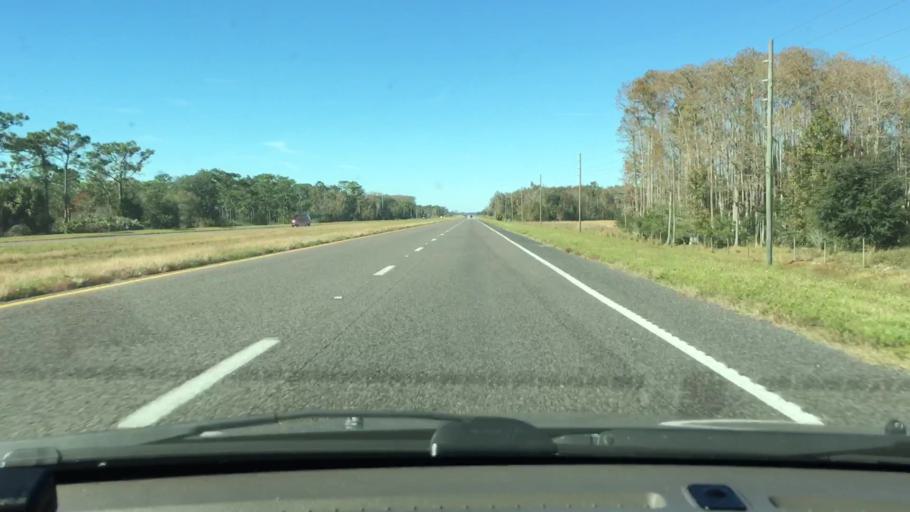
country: US
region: Florida
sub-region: Brevard County
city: June Park
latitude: 28.1225
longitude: -80.9570
